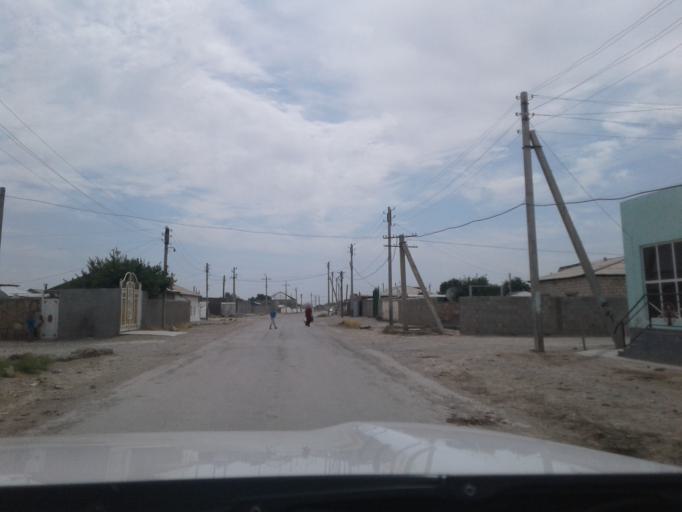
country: TM
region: Balkan
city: Serdar
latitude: 38.9892
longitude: 56.2731
